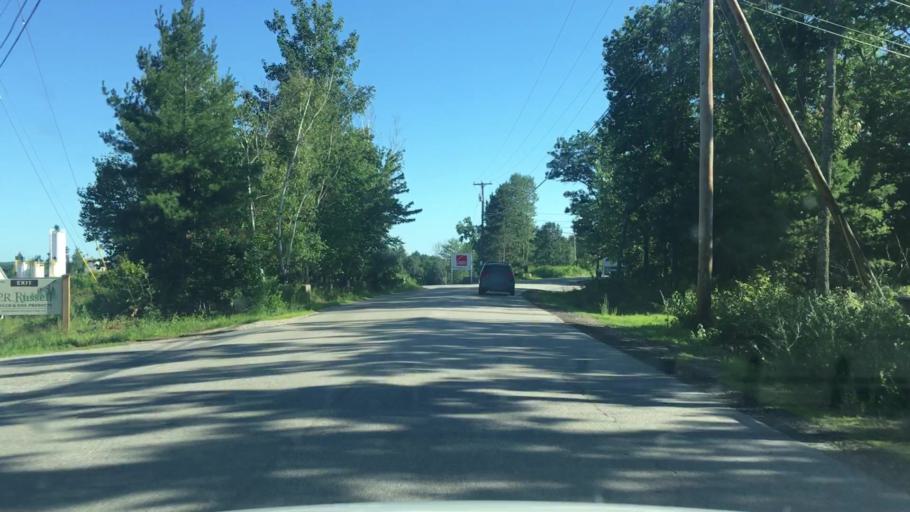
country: US
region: New Hampshire
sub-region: Rockingham County
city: Brentwood
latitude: 43.0037
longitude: -71.0136
